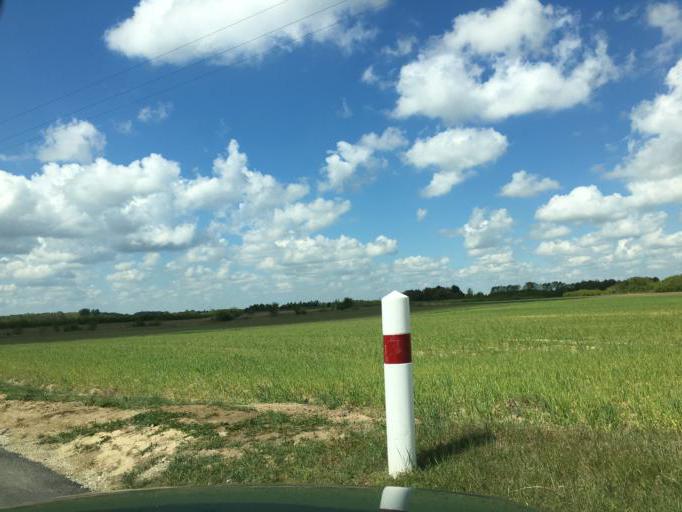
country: FR
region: Centre
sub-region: Departement du Loiret
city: Mareau-aux-Pres
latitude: 47.8274
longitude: 1.8008
